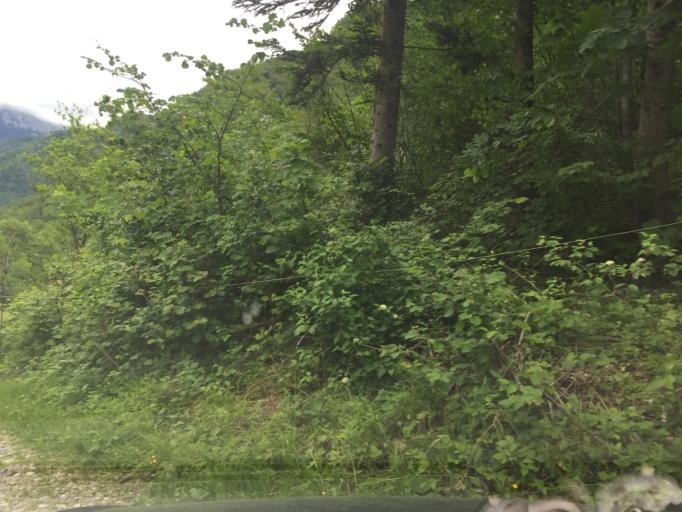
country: SI
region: Tolmin
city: Tolmin
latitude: 46.1702
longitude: 13.8376
